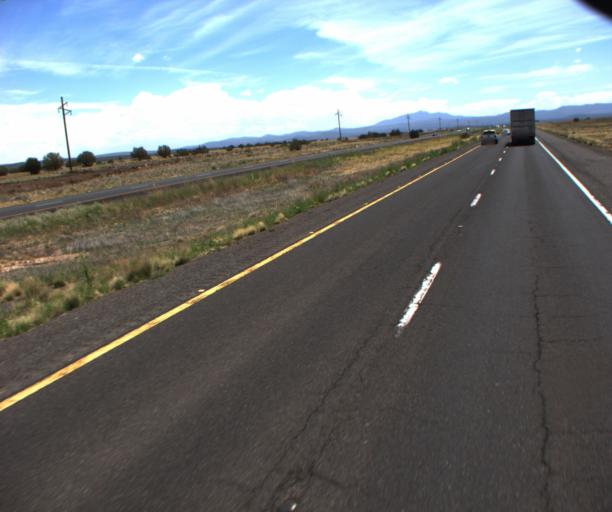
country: US
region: Arizona
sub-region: Yavapai County
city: Paulden
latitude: 35.2251
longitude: -112.5642
